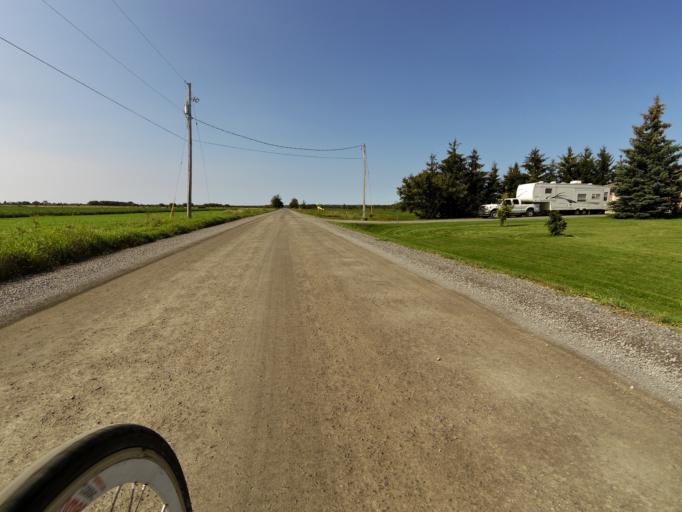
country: CA
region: Ontario
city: Arnprior
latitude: 45.3690
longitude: -76.1362
